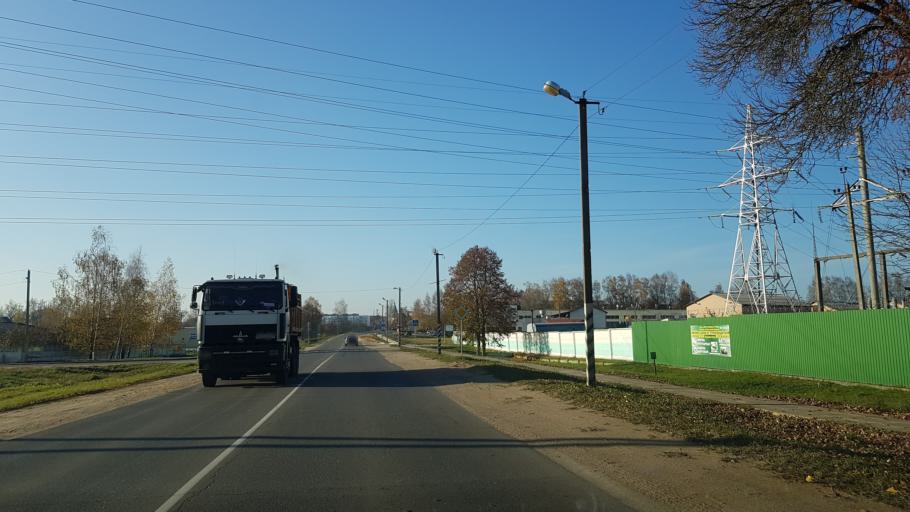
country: BY
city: Fanipol
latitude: 53.7361
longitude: 27.3252
